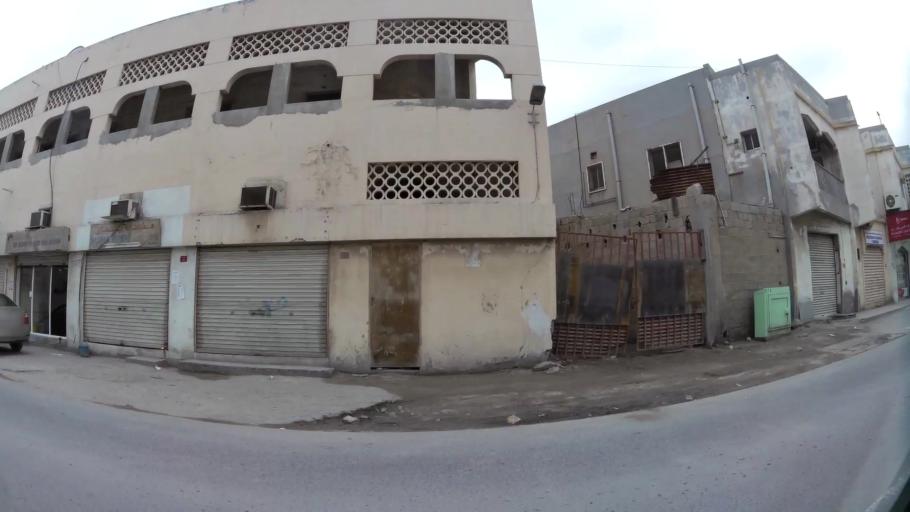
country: BH
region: Northern
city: Sitrah
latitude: 26.1673
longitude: 50.6148
